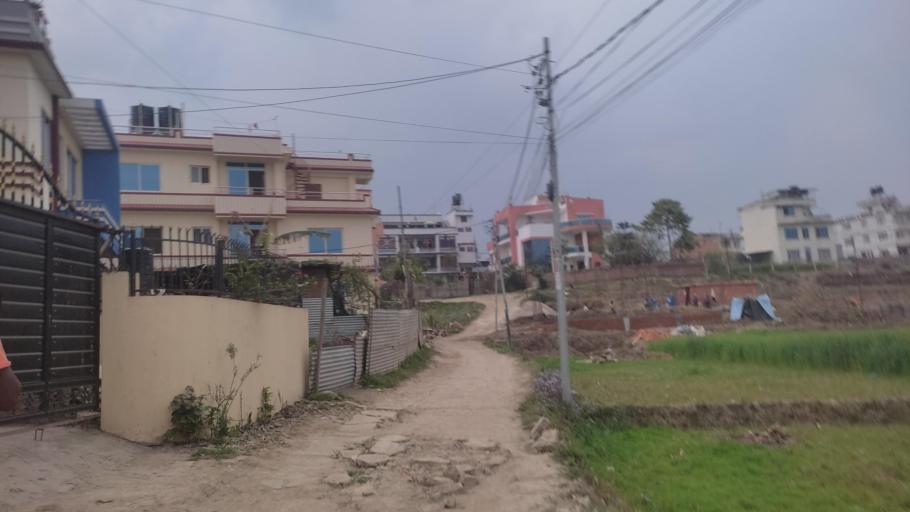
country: NP
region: Central Region
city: Kirtipur
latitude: 27.6635
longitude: 85.2735
